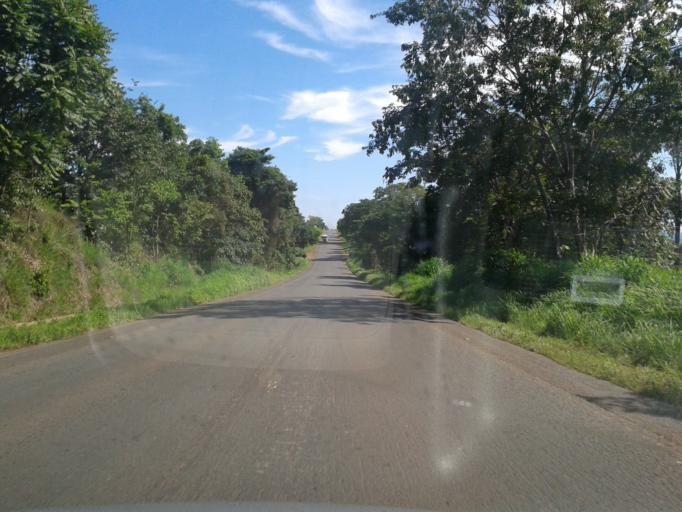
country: BR
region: Goias
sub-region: Piracanjuba
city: Piracanjuba
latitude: -17.2226
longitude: -48.7124
